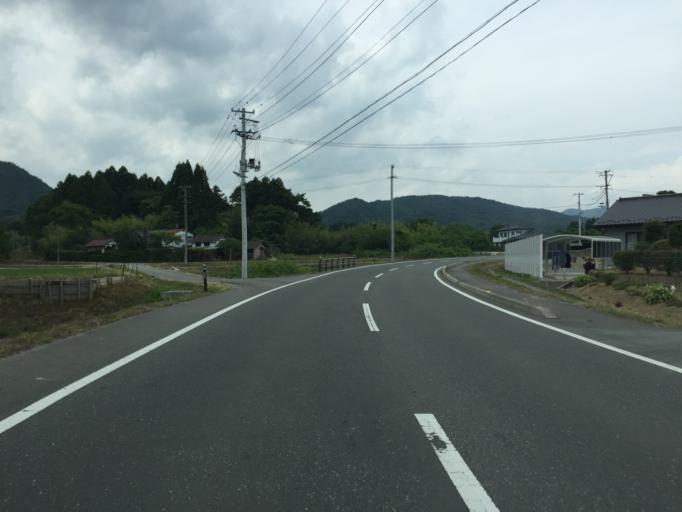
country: JP
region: Miyagi
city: Marumori
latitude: 37.8182
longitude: 140.8868
